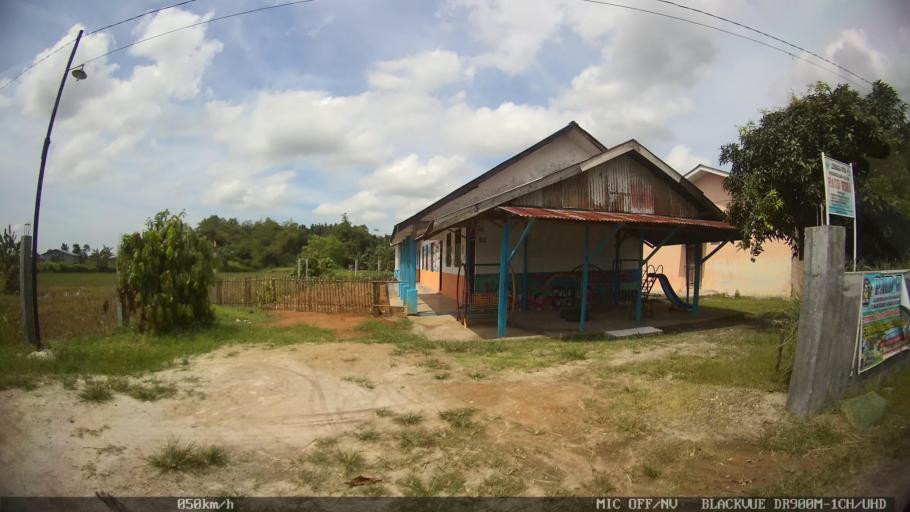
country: ID
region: North Sumatra
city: Percut
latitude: 3.5688
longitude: 98.8521
